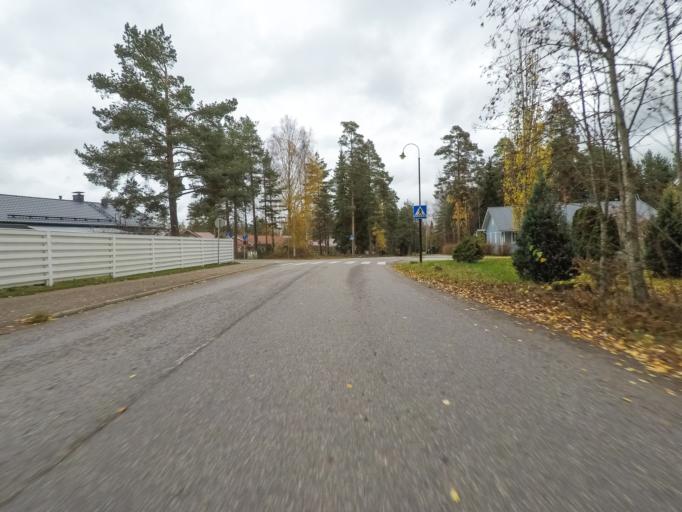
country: FI
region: Uusimaa
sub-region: Porvoo
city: Porvoo
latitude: 60.4108
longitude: 25.6757
